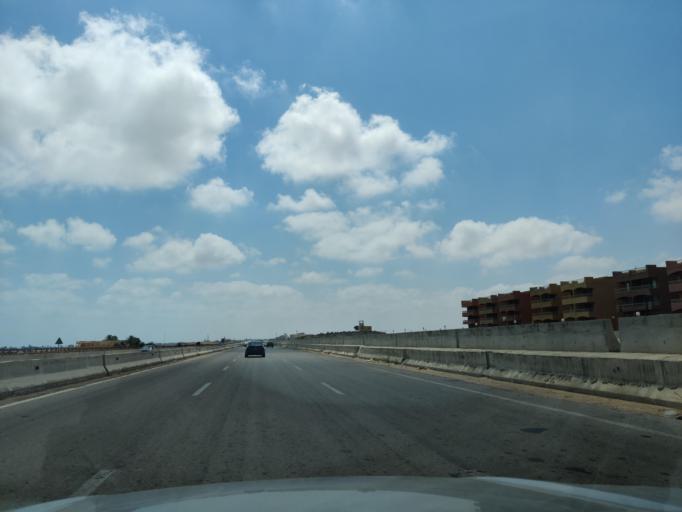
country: EG
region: Muhafazat Matruh
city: Al `Alamayn
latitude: 30.8218
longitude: 29.0022
